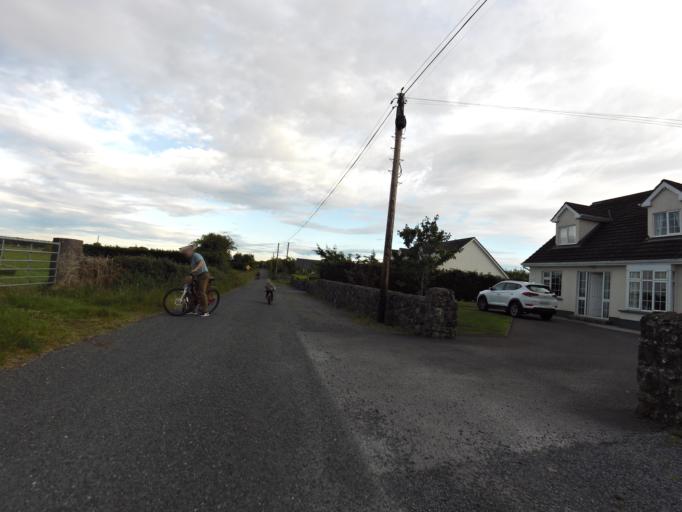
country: IE
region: Connaught
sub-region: County Galway
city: Athenry
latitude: 53.2890
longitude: -8.7143
